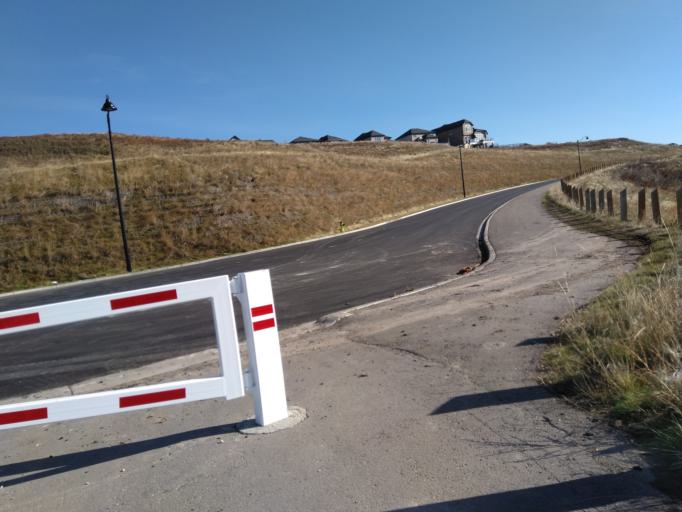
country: CA
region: Alberta
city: Calgary
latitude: 51.1779
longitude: -114.1270
